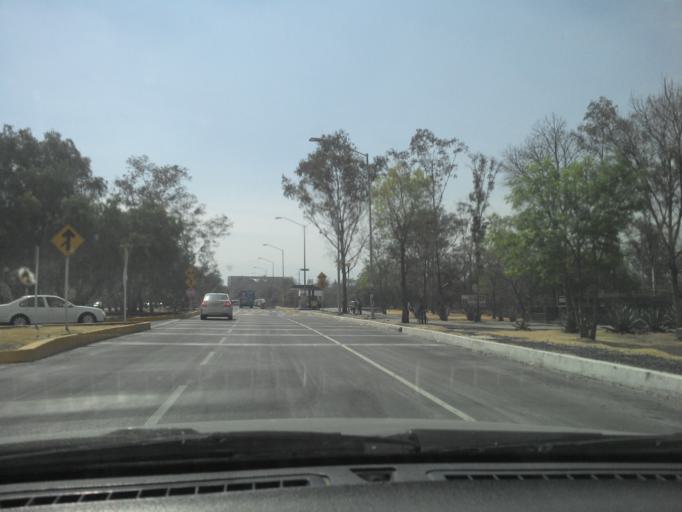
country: MX
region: Mexico City
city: Tlalpan
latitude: 19.3152
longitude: -99.1864
